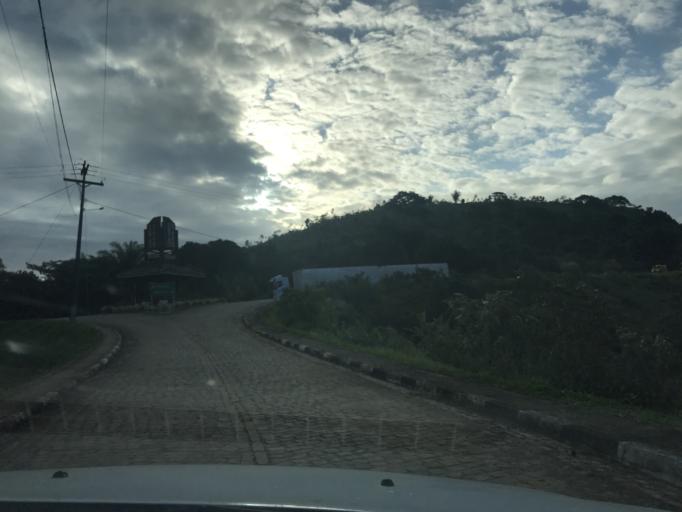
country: BR
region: Bahia
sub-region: Gandu
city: Gandu
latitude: -13.8973
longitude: -39.4774
